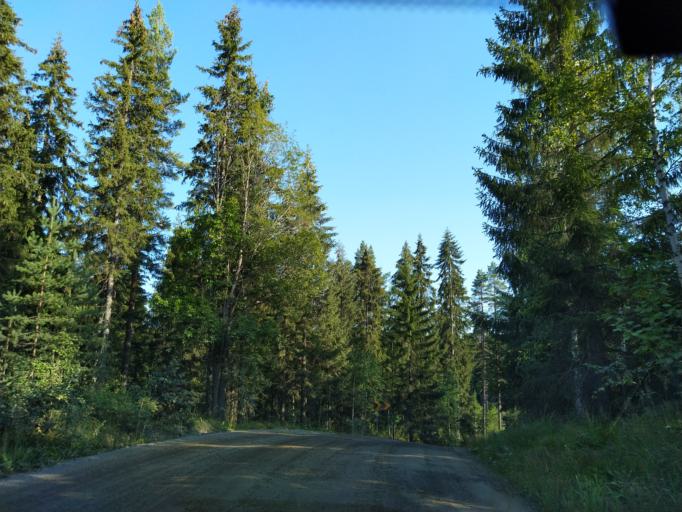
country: FI
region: Central Finland
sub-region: Jaemsae
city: Kuhmoinen
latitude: 61.6295
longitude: 25.0931
